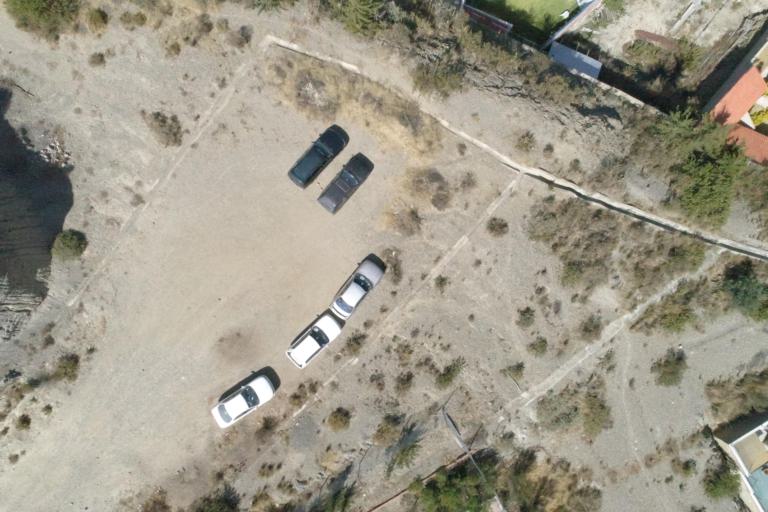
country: BO
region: La Paz
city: La Paz
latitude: -16.5338
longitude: -68.0692
